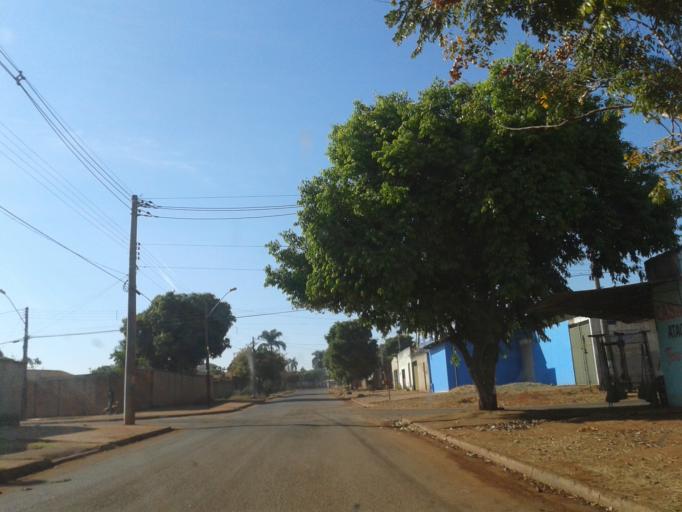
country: BR
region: Goias
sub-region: Goiania
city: Goiania
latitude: -16.6513
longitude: -49.3501
